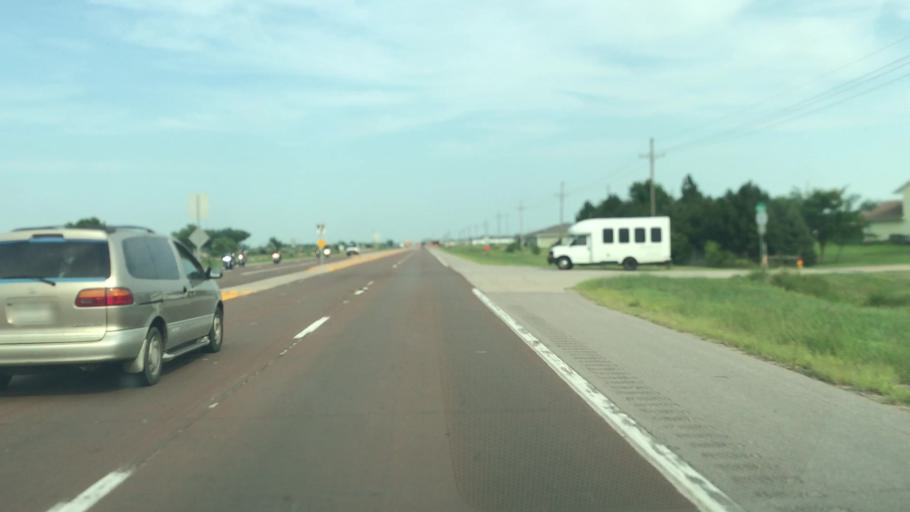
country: US
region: Nebraska
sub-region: Hall County
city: Grand Island
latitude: 40.9578
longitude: -98.4043
